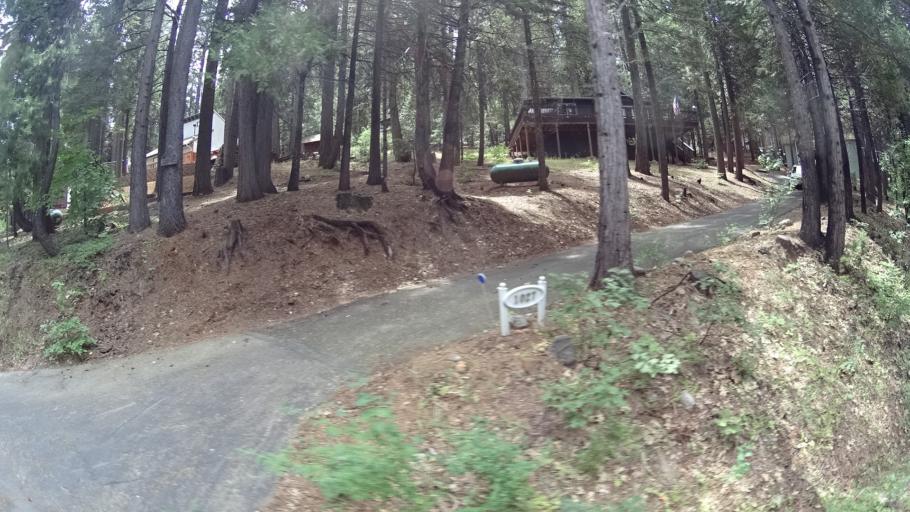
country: US
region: California
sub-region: Calaveras County
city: Arnold
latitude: 38.2530
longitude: -120.3474
